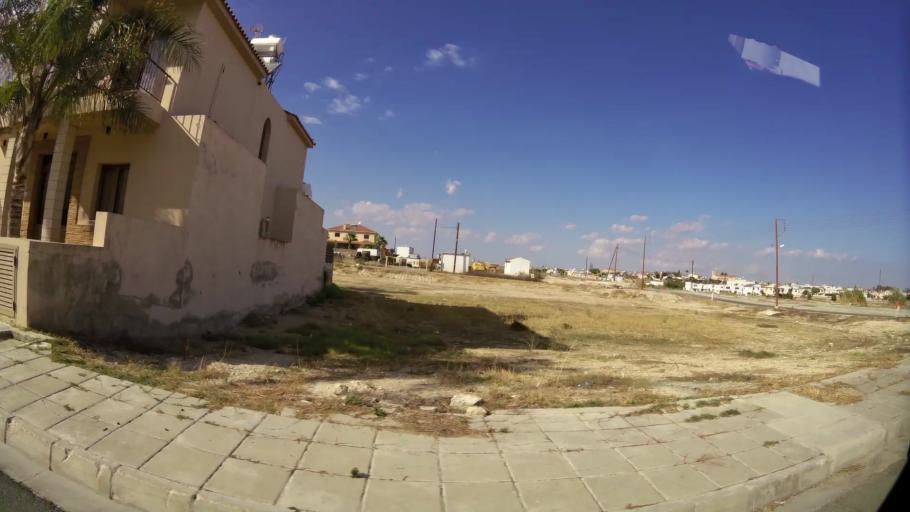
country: CY
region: Larnaka
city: Livadia
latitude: 34.9419
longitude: 33.6211
